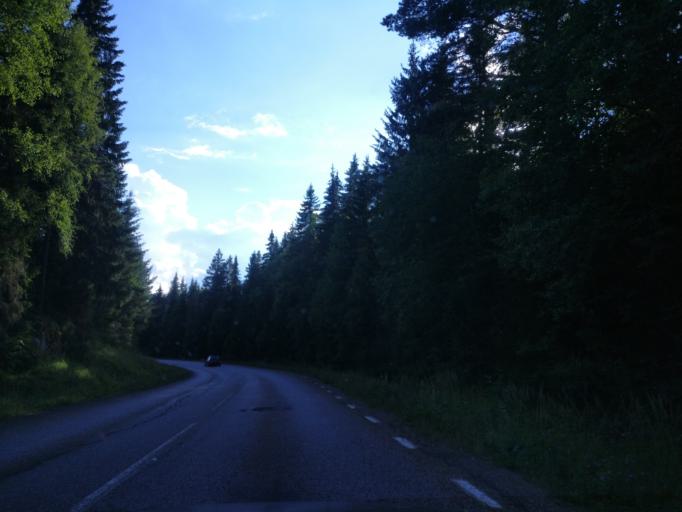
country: SE
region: Dalarna
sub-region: Ludvika Kommun
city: Ludvika
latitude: 60.2705
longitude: 15.0657
